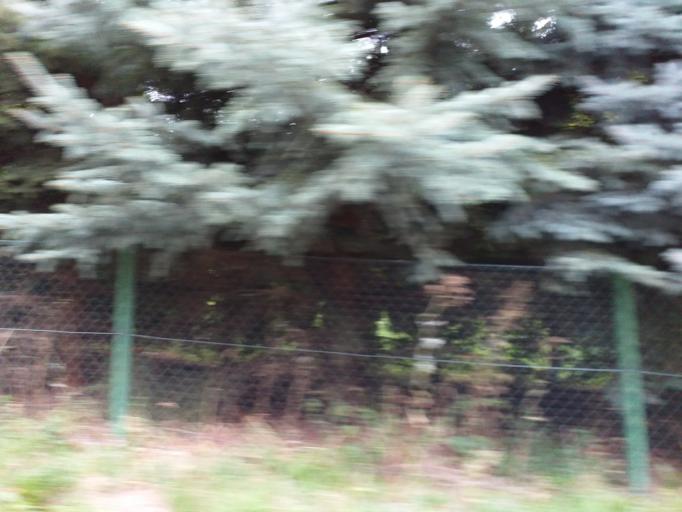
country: PL
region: Lower Silesian Voivodeship
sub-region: Powiat lubanski
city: Lesna
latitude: 51.0178
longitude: 15.3133
